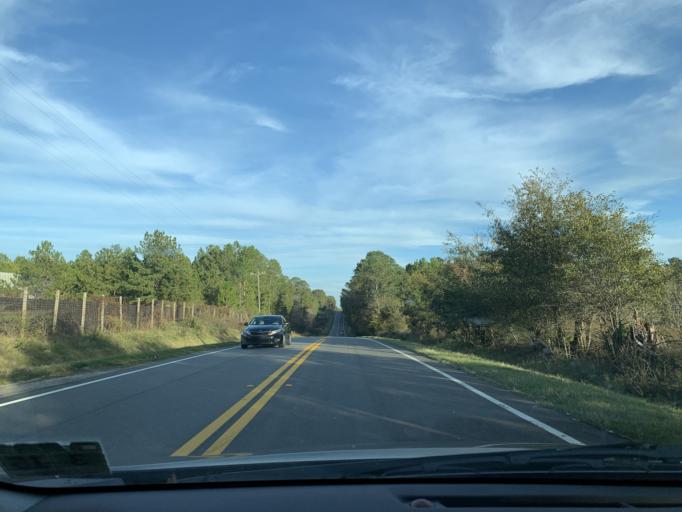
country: US
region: Georgia
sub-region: Irwin County
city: Ocilla
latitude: 31.5957
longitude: -83.1459
